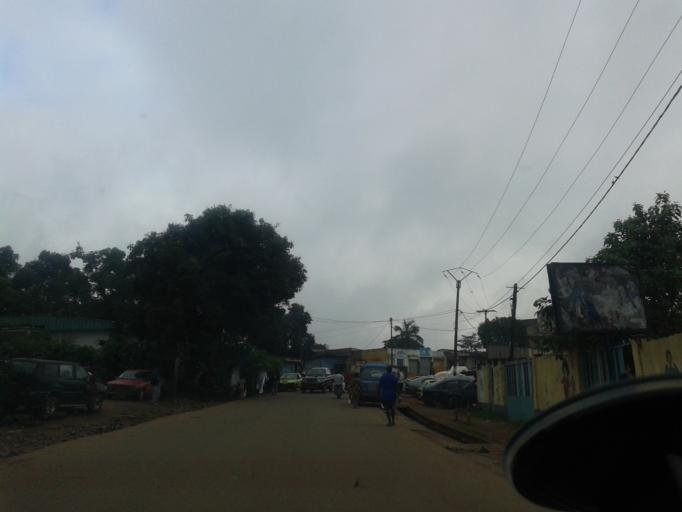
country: CM
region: Centre
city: Yaounde
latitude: 3.9090
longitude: 11.5281
